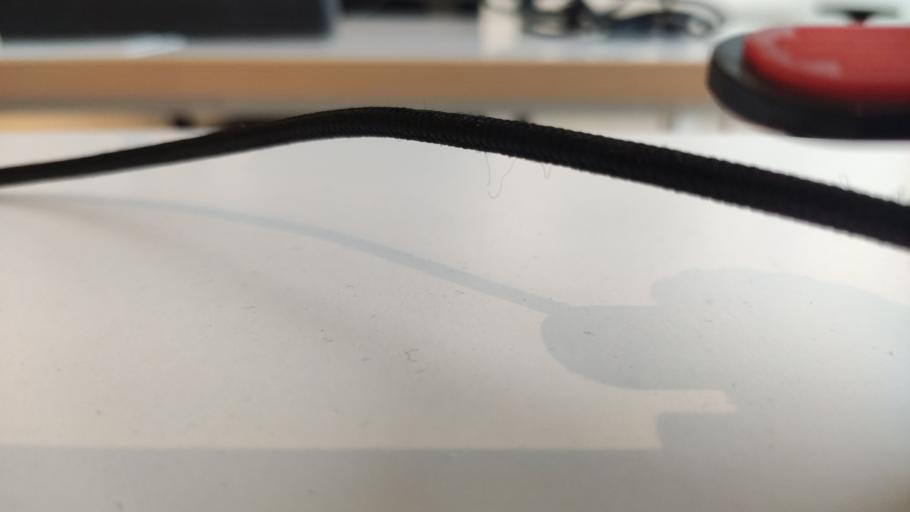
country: RU
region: Moskovskaya
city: Klin
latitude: 56.3612
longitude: 36.7592
